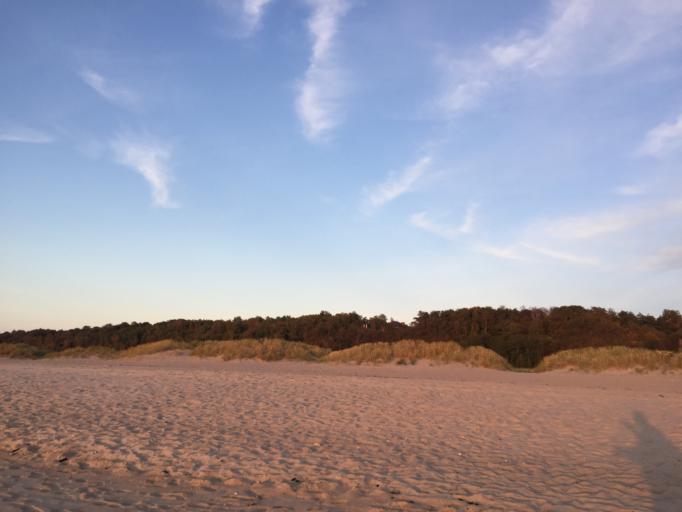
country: RU
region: Kaliningrad
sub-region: Gorod Kaliningrad
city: Yantarnyy
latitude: 54.8846
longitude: 19.9308
